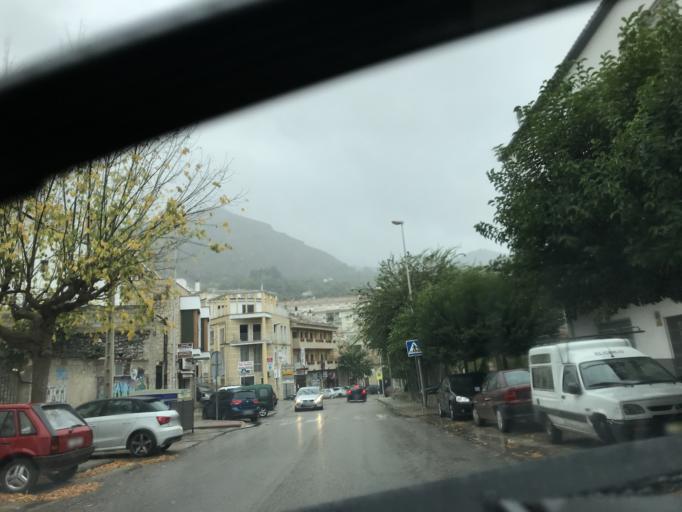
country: ES
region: Andalusia
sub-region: Provincia de Jaen
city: Cazorla
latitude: 37.9150
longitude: -3.0067
